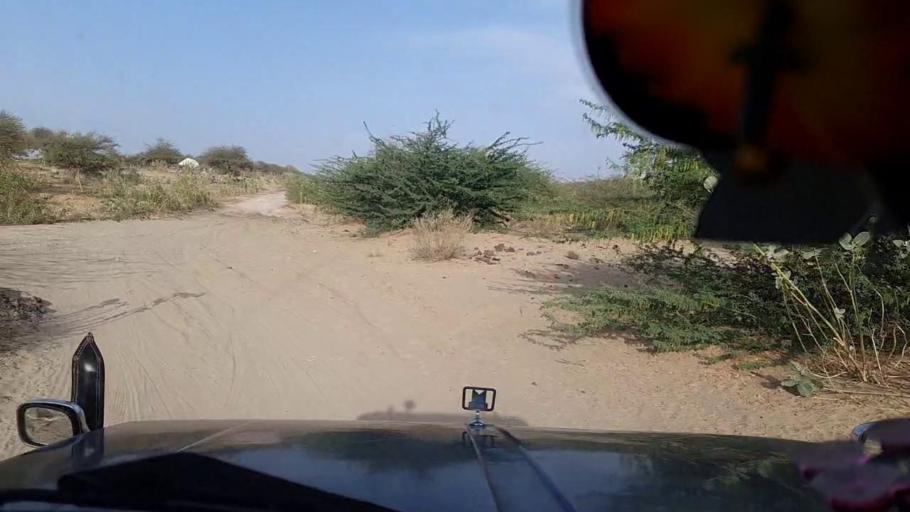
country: PK
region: Sindh
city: Diplo
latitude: 24.5511
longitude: 69.4594
